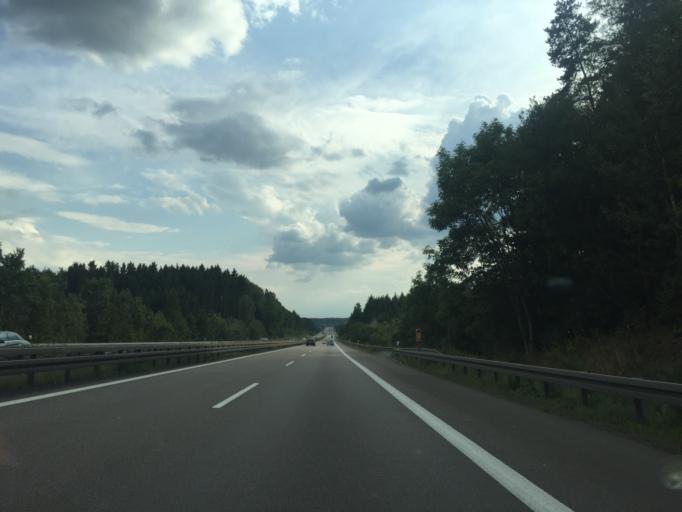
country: DE
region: Bavaria
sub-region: Upper Palatinate
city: Windischeschenbach
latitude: 49.7929
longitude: 12.1746
